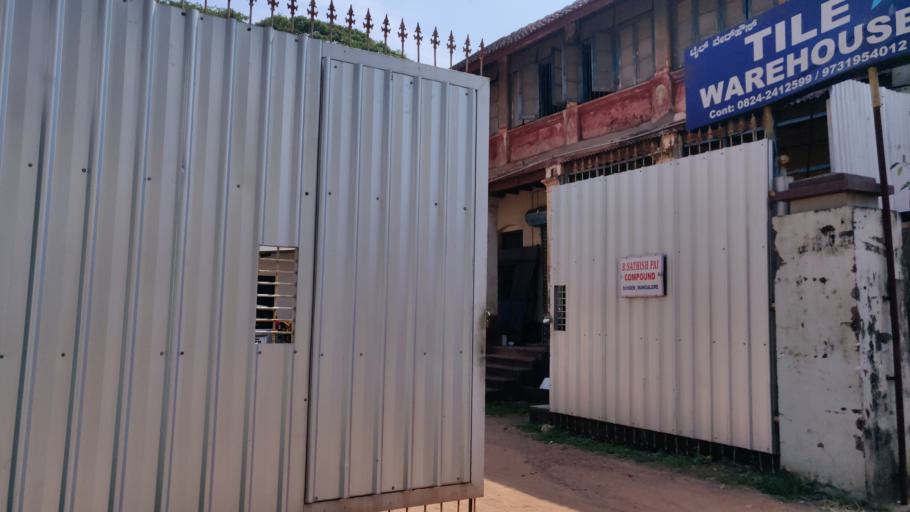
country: IN
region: Karnataka
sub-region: Dakshina Kannada
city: Ullal
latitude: 12.8619
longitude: 74.8337
